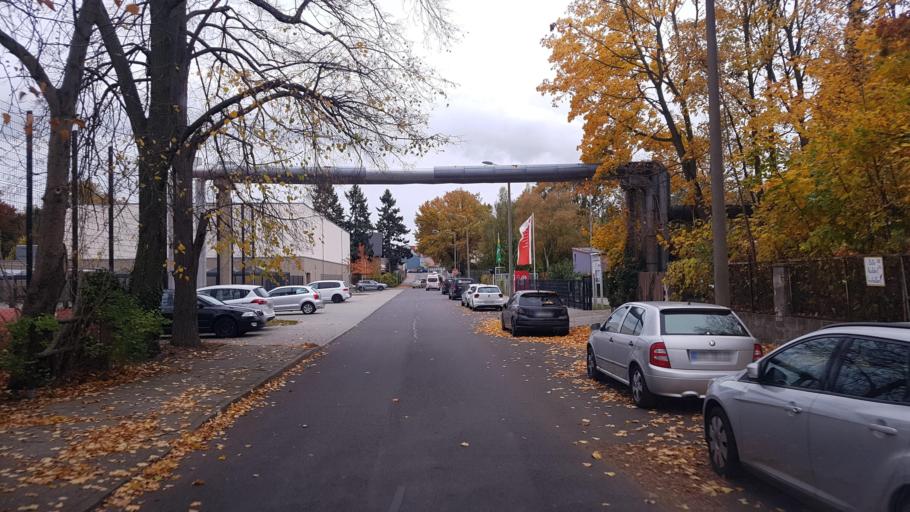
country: DE
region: Brandenburg
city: Spremberg
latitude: 51.5732
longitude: 14.3710
